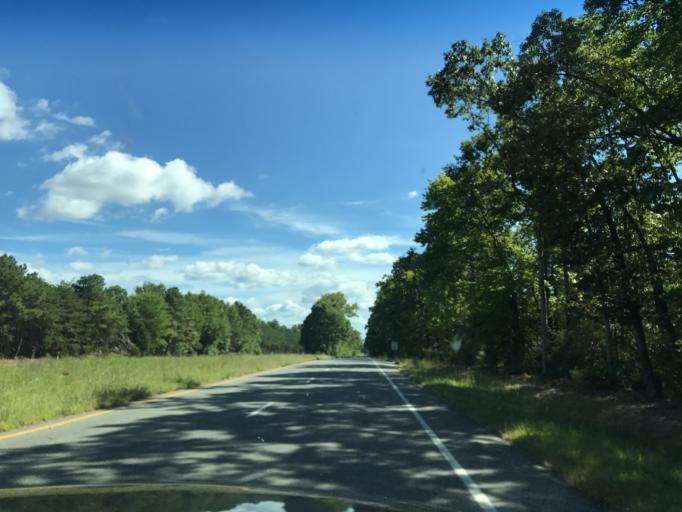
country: US
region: Virginia
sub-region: Essex County
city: Tappahannock
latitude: 37.7980
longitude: -76.7728
